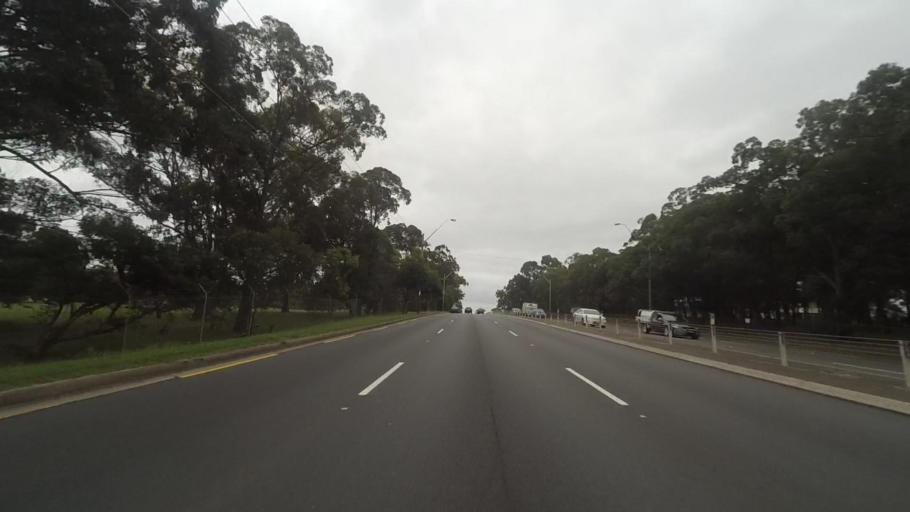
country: AU
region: New South Wales
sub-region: Auburn
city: Berala
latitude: -33.8753
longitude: 151.0416
